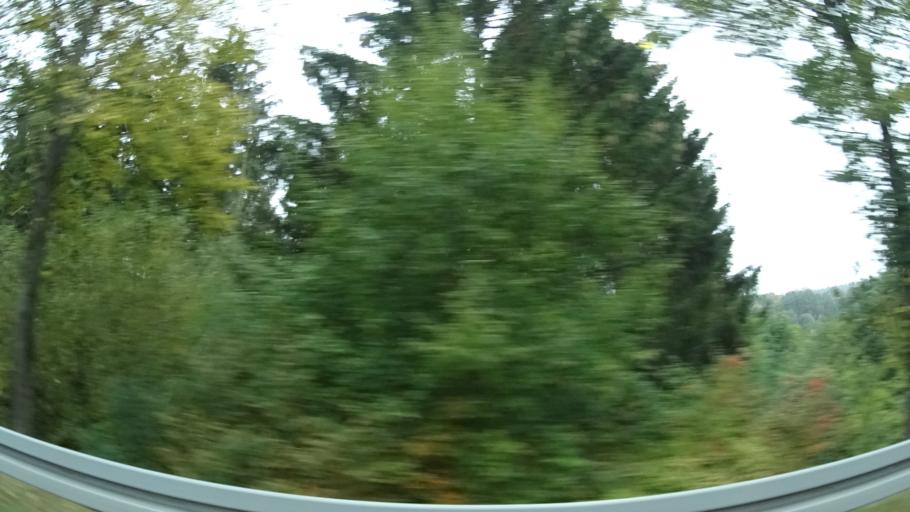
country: DE
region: Hesse
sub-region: Regierungsbezirk Kassel
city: Hilders
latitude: 50.5657
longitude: 10.0053
